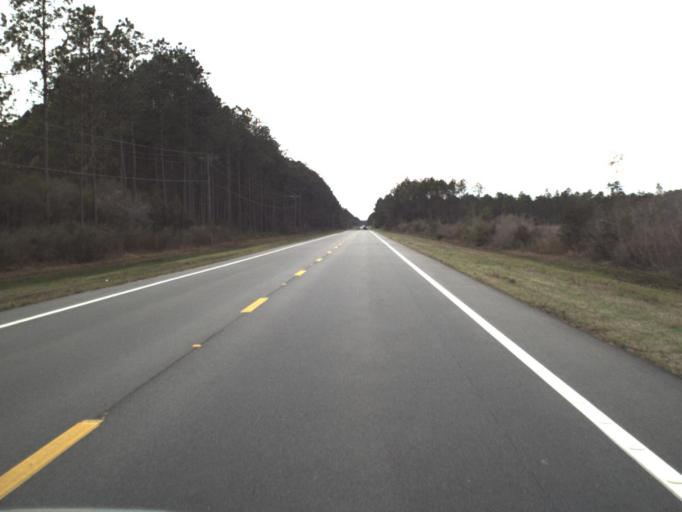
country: US
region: Florida
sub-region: Gulf County
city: Wewahitchka
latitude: 30.1417
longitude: -85.2764
